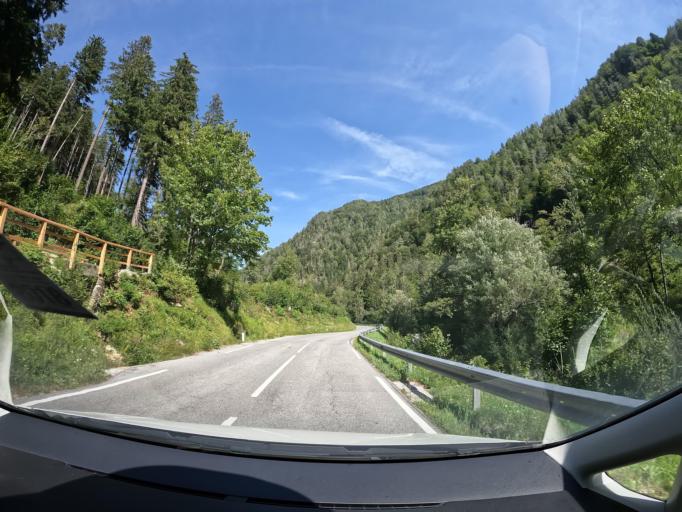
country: SI
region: Zirovnica
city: Zirovnica
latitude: 46.4403
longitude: 14.1594
